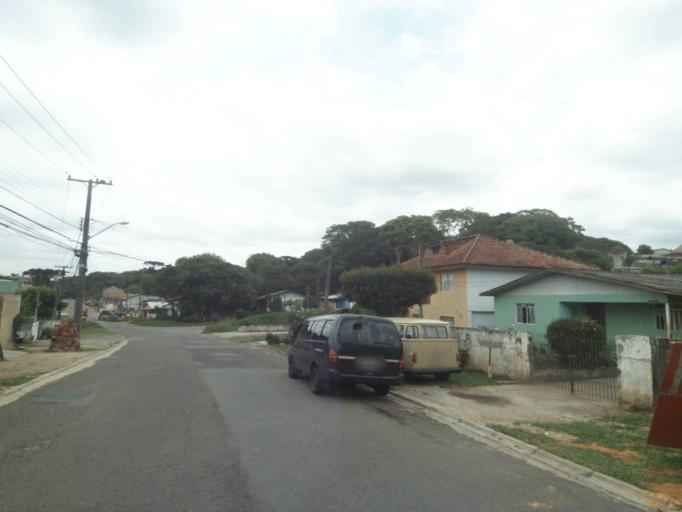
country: BR
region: Parana
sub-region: Curitiba
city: Curitiba
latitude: -25.3864
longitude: -49.2919
